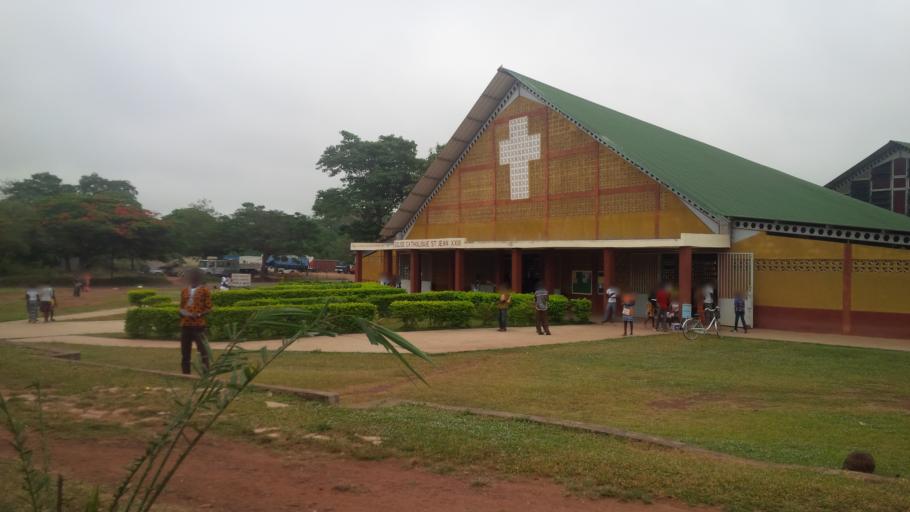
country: CI
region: Zanzan
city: Tanda
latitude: 7.8004
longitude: -3.1635
